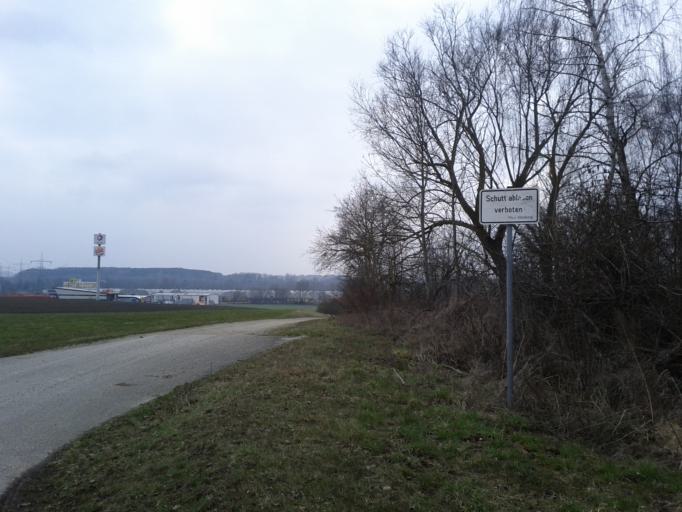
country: DE
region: Bavaria
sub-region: Swabia
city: Wasserburg
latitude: 48.4302
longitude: 10.2922
